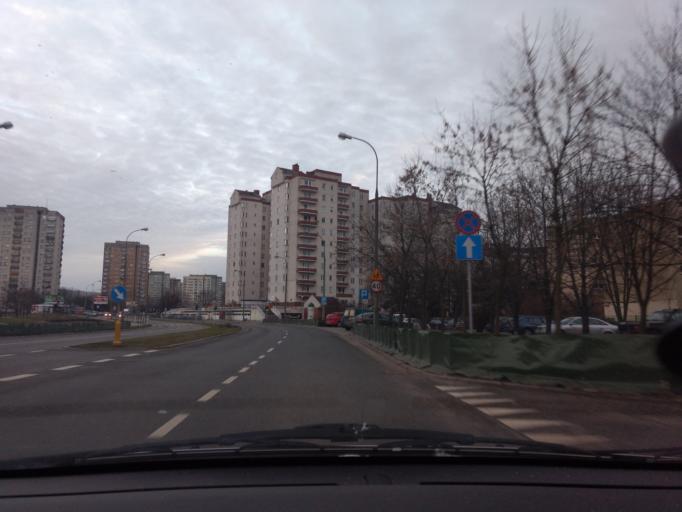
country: PL
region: Masovian Voivodeship
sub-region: Warszawa
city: Praga Poludnie
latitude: 52.2281
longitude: 21.0866
